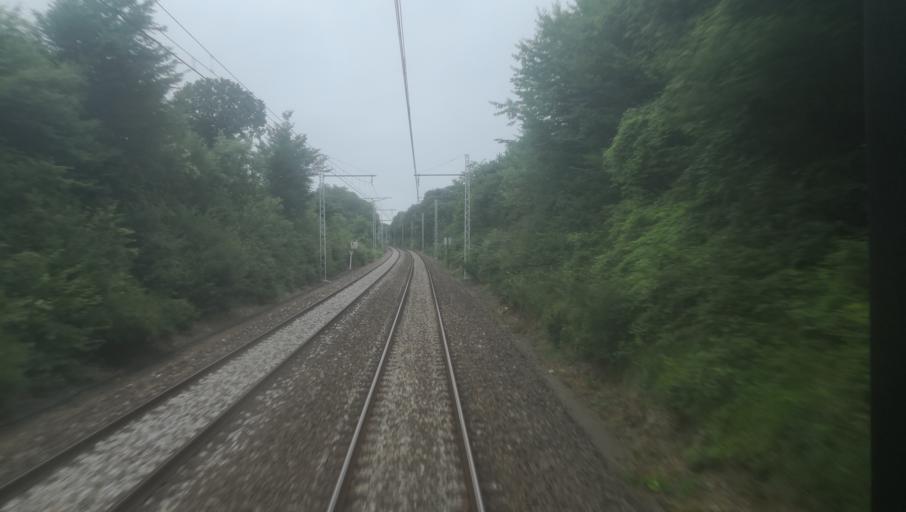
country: FR
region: Centre
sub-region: Departement de l'Indre
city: Saint-Marcel
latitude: 46.6652
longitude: 1.5365
